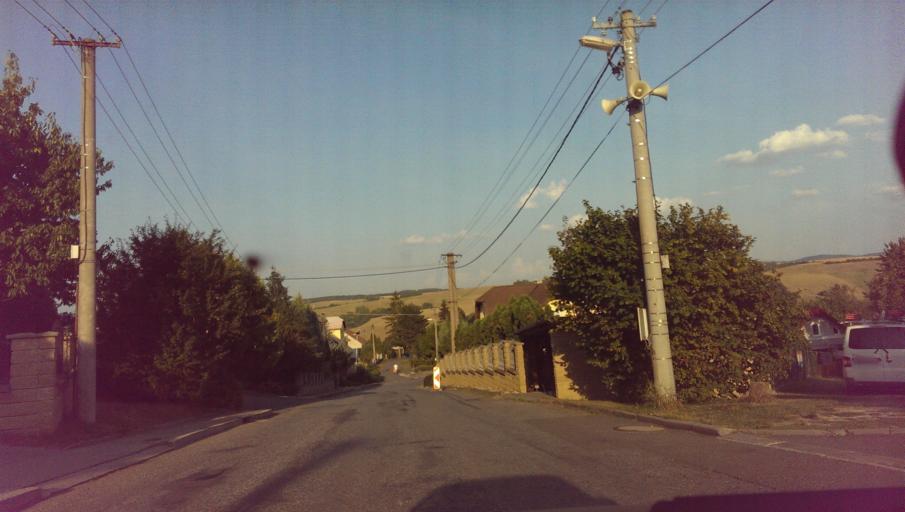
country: CZ
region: Zlin
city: Slusovice
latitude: 49.2379
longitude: 17.7831
